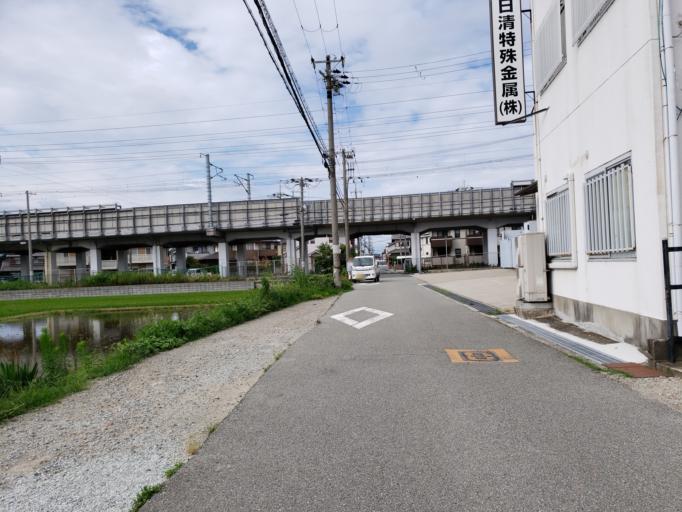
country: JP
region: Hyogo
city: Kakogawacho-honmachi
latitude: 34.7539
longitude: 134.8161
